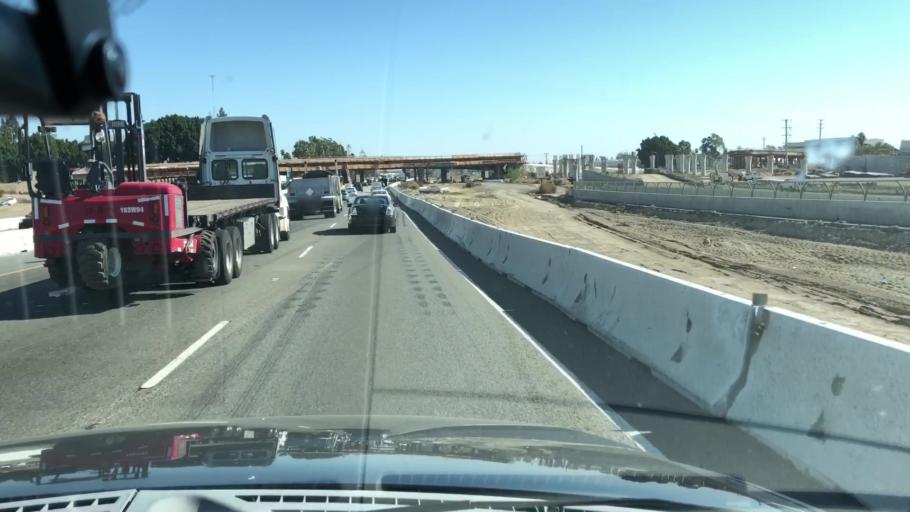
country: US
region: California
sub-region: Los Angeles County
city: La Mirada
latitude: 33.8856
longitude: -118.0317
